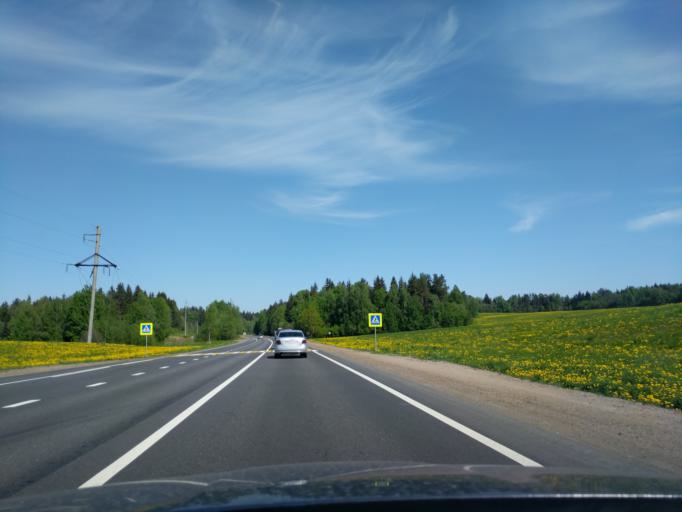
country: BY
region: Minsk
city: Bal'shavik
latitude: 54.1008
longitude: 27.5334
